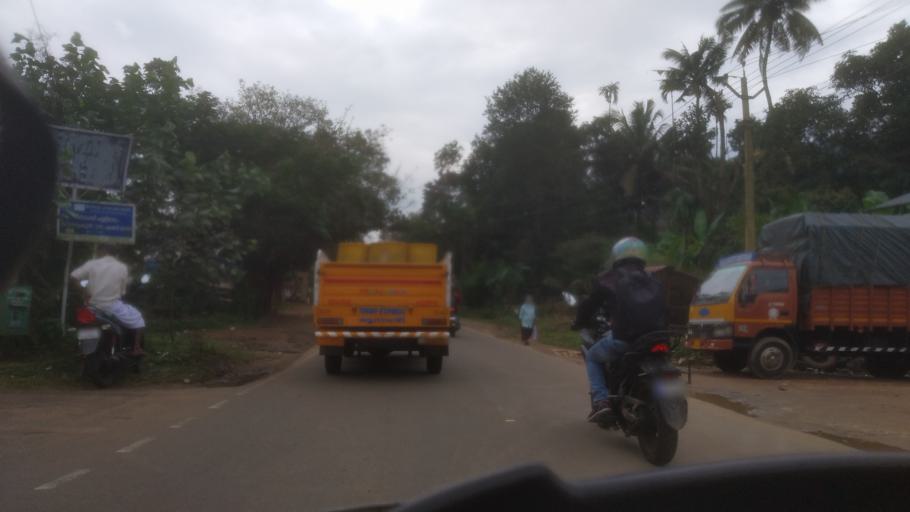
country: IN
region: Kerala
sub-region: Idukki
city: Munnar
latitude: 9.9922
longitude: 76.9795
